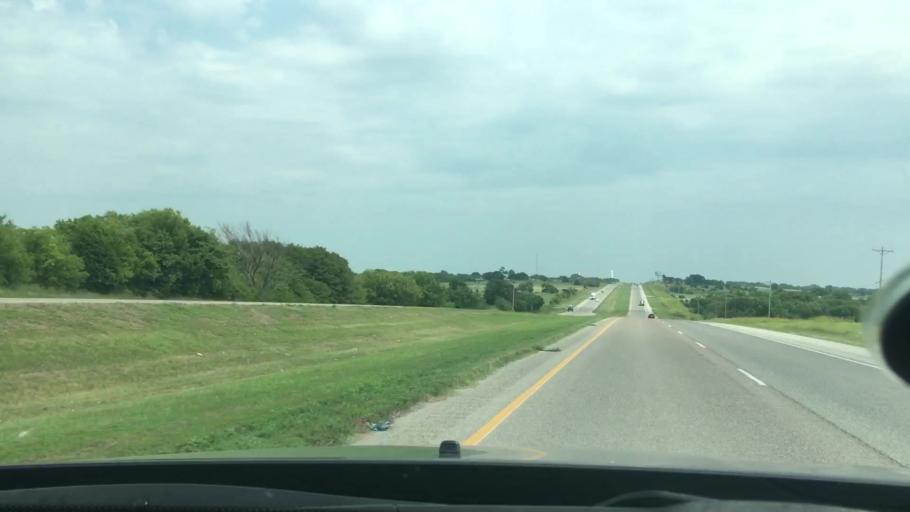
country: US
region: Oklahoma
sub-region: Murray County
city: Davis
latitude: 34.5059
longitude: -97.0762
